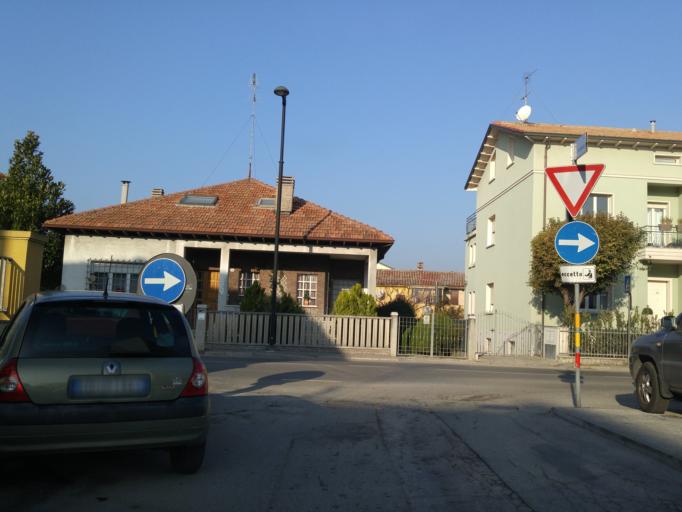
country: IT
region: The Marches
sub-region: Provincia di Pesaro e Urbino
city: Fano
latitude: 43.8399
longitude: 13.0110
